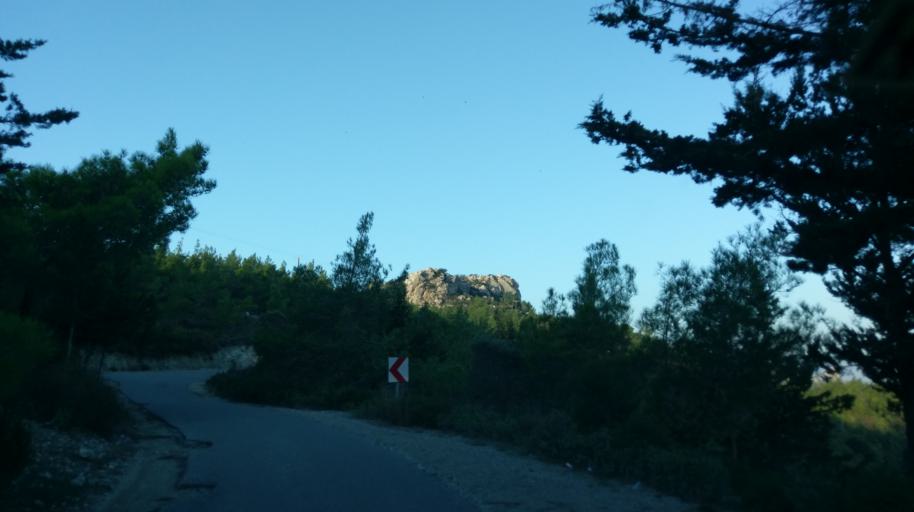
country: CY
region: Ammochostos
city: Trikomo
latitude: 35.3934
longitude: 33.9039
